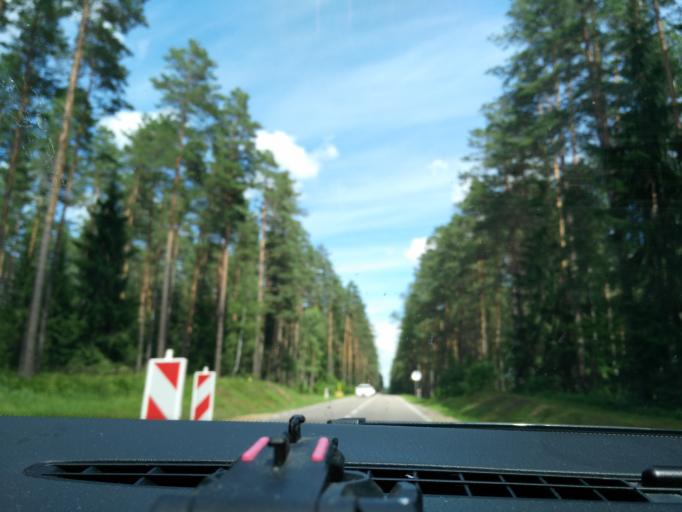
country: PL
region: Podlasie
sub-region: Powiat sejnenski
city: Krasnopol
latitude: 53.9647
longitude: 23.2387
